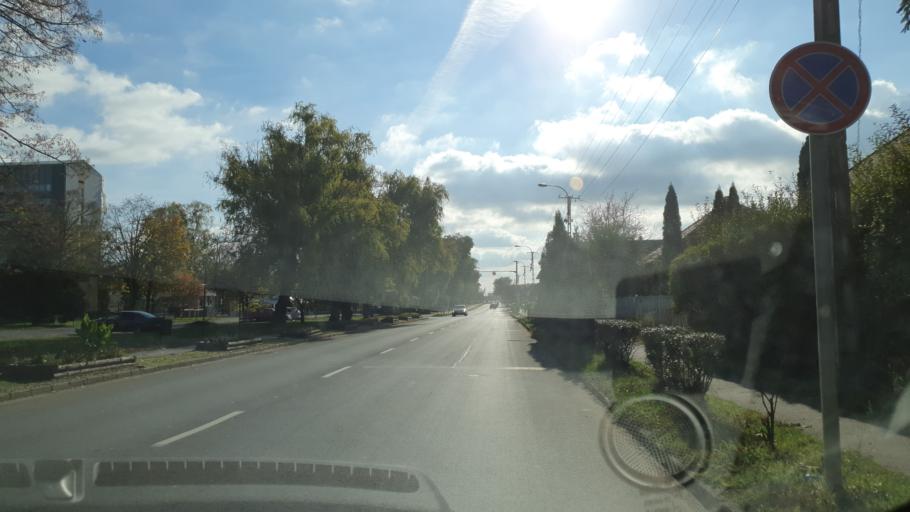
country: HU
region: Szabolcs-Szatmar-Bereg
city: Kisvarda
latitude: 48.2090
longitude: 22.0876
